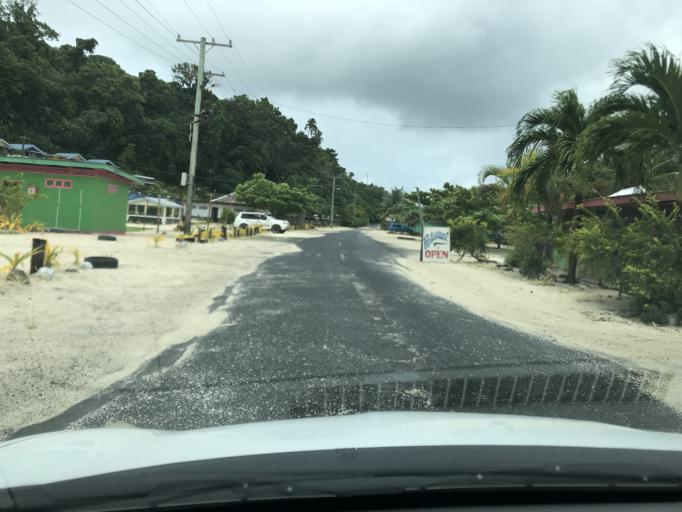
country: WS
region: Va`a-o-Fonoti
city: Samamea
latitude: -14.0458
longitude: -171.4468
